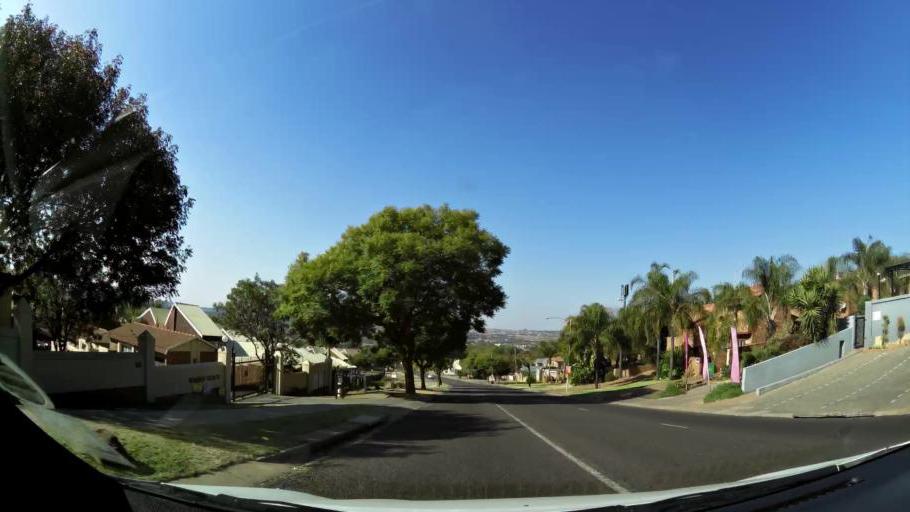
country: ZA
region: Gauteng
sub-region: City of Tshwane Metropolitan Municipality
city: Centurion
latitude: -25.8192
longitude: 28.2905
